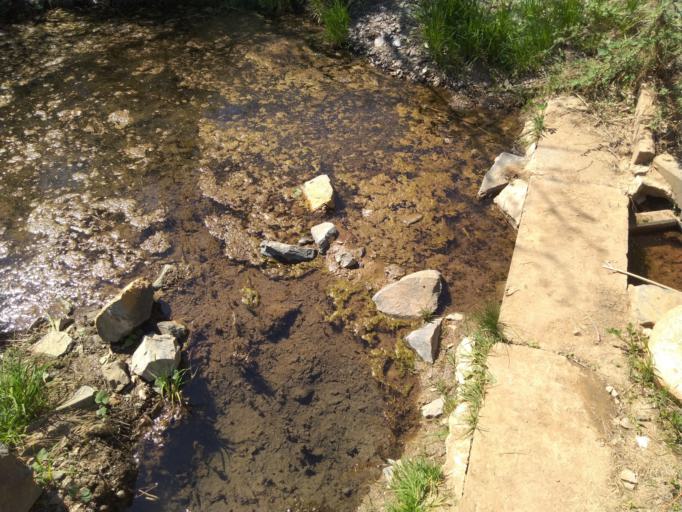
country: RU
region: Orenburg
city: Orsk
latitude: 51.1365
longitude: 58.4873
